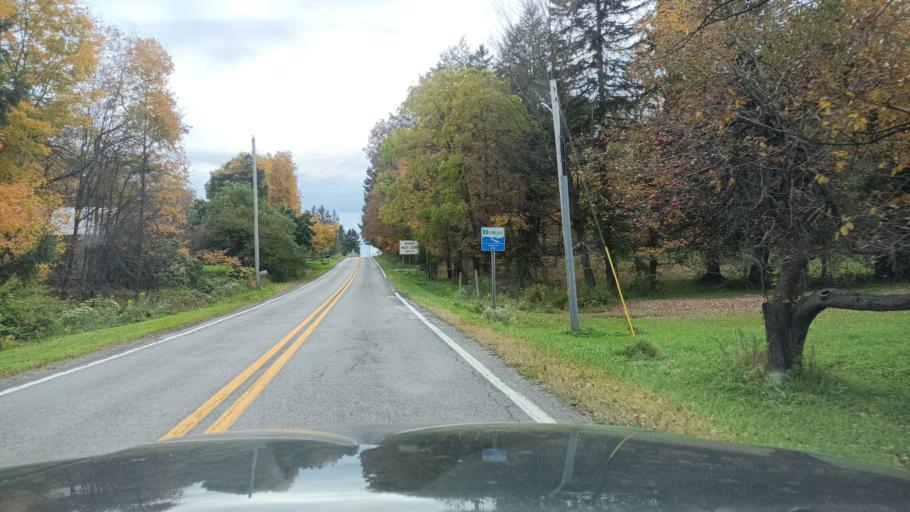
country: US
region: West Virginia
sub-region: Preston County
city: Terra Alta
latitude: 39.3126
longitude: -79.5881
